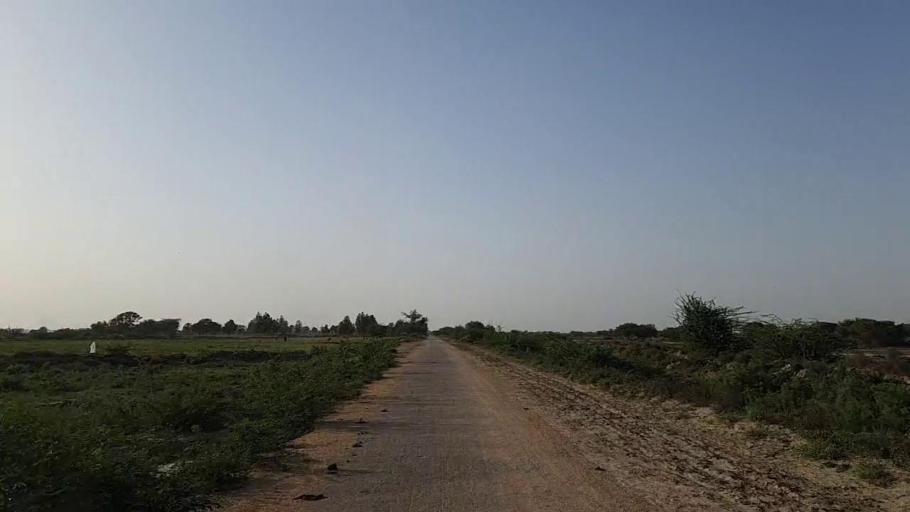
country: PK
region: Sindh
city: Jati
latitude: 24.3259
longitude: 68.1635
